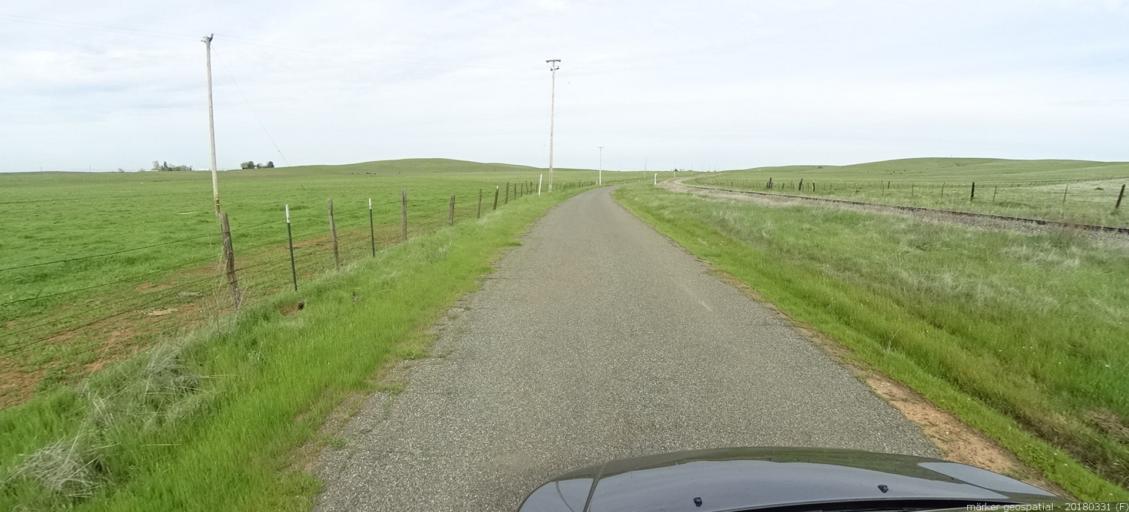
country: US
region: California
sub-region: El Dorado County
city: El Dorado Hills
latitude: 38.6154
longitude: -121.0765
